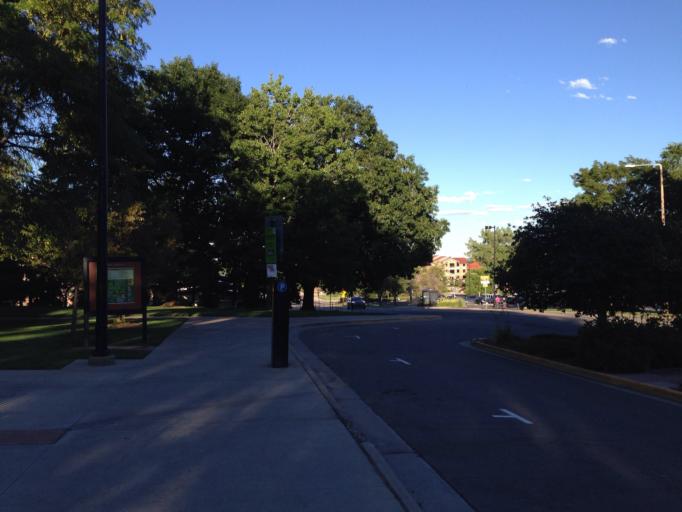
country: US
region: Colorado
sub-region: Boulder County
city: Boulder
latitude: 40.0041
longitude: -105.2670
